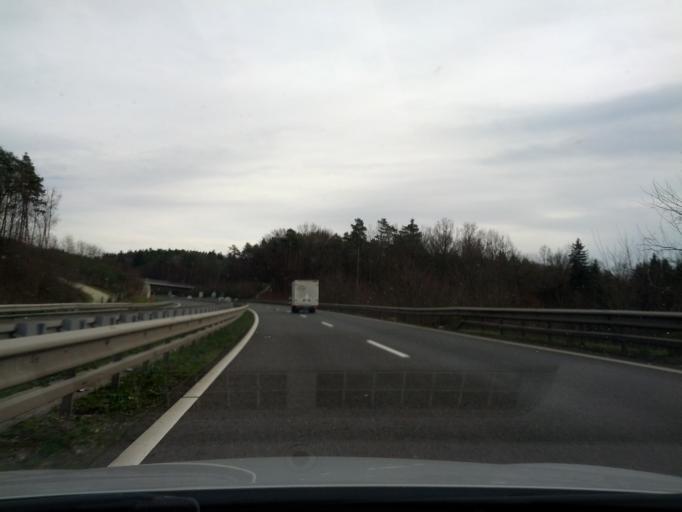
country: SI
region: Sveti Jurij
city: Sveti Jurij ob Scavnici
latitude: 46.5767
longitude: 16.0465
